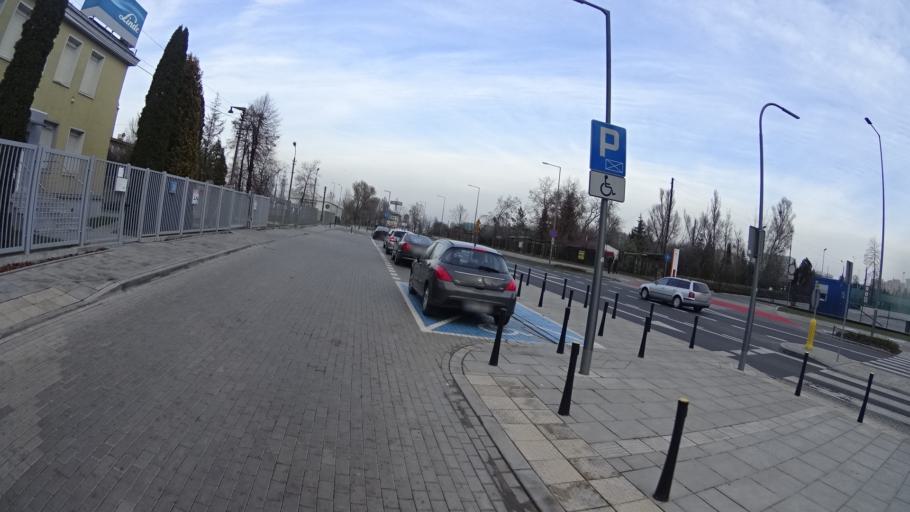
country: PL
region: Masovian Voivodeship
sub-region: Warszawa
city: Bielany
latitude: 52.2970
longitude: 20.9316
